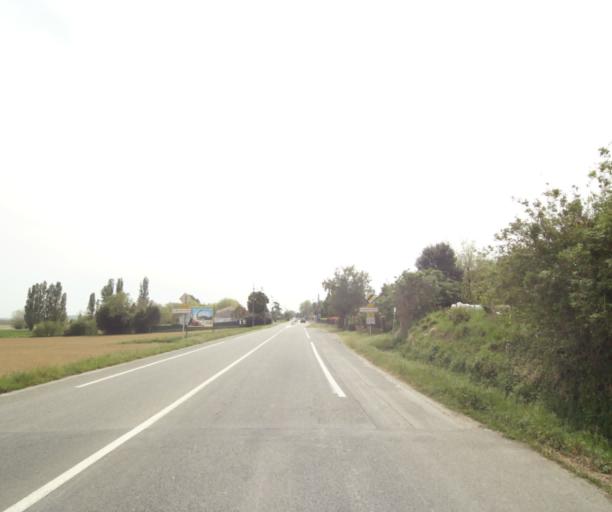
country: FR
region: Midi-Pyrenees
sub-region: Departement de la Haute-Garonne
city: Pompertuzat
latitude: 43.4979
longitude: 1.5169
